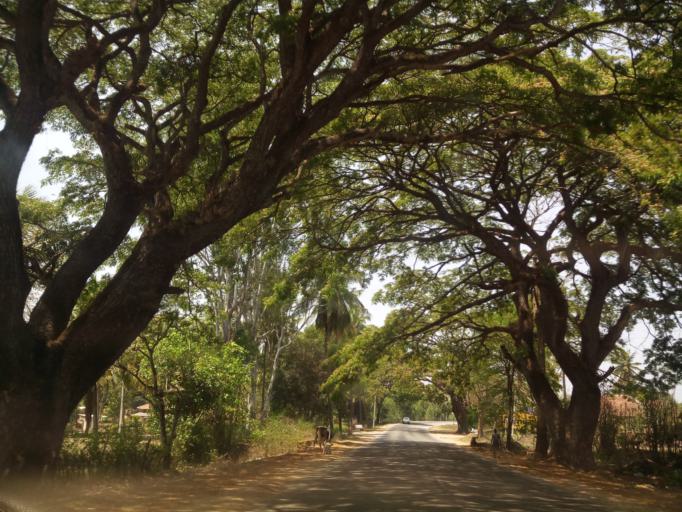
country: IN
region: Karnataka
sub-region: Hassan
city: Alur
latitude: 12.9477
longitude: 75.9491
